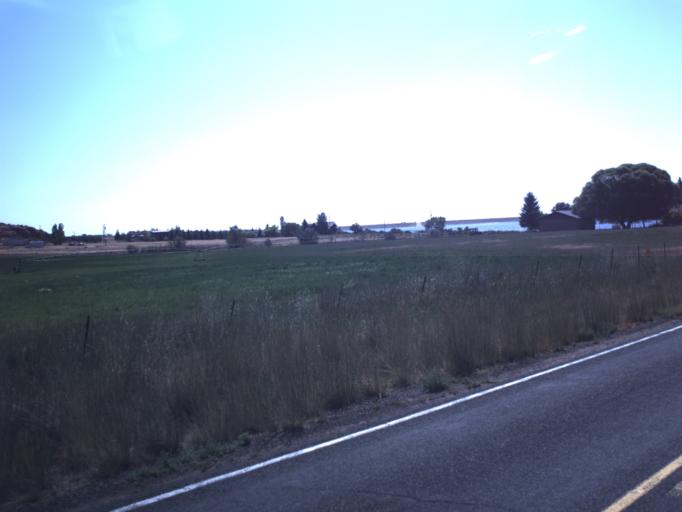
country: US
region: Utah
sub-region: Duchesne County
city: Duchesne
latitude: 40.3042
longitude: -110.2406
